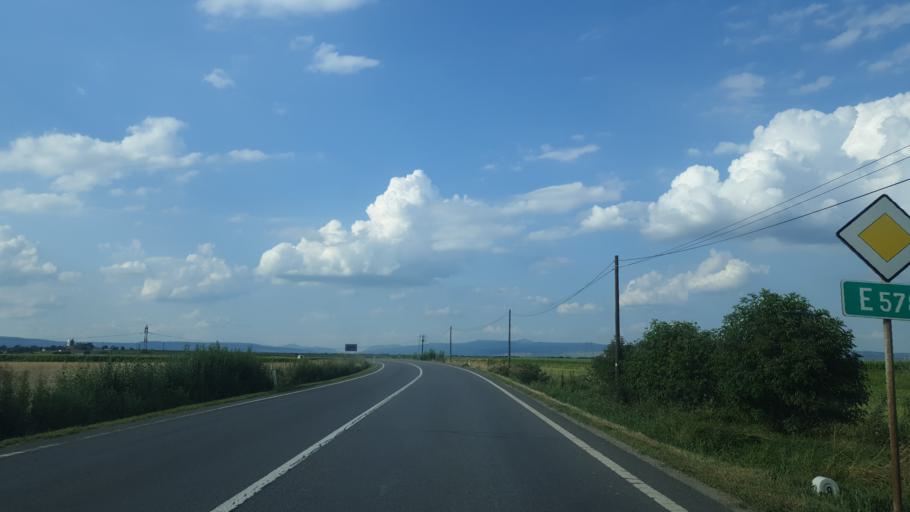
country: RO
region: Covasna
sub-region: Comuna Chichis
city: Chichis
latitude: 45.7988
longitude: 25.8046
